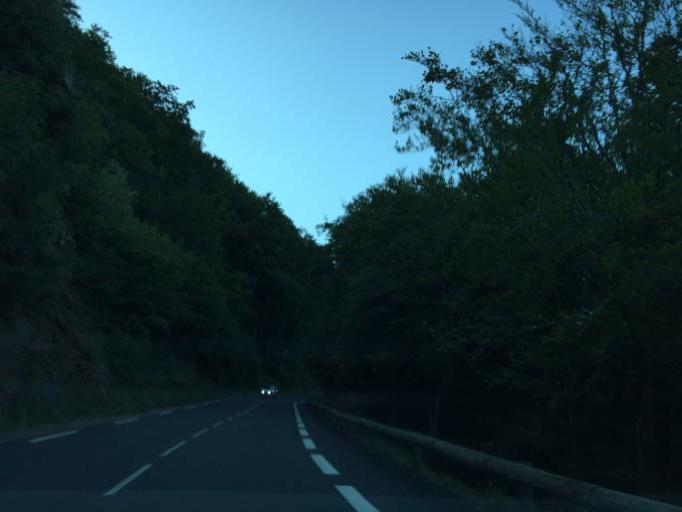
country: FR
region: Auvergne
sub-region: Departement de la Haute-Loire
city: Bains
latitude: 44.9826
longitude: 3.6745
